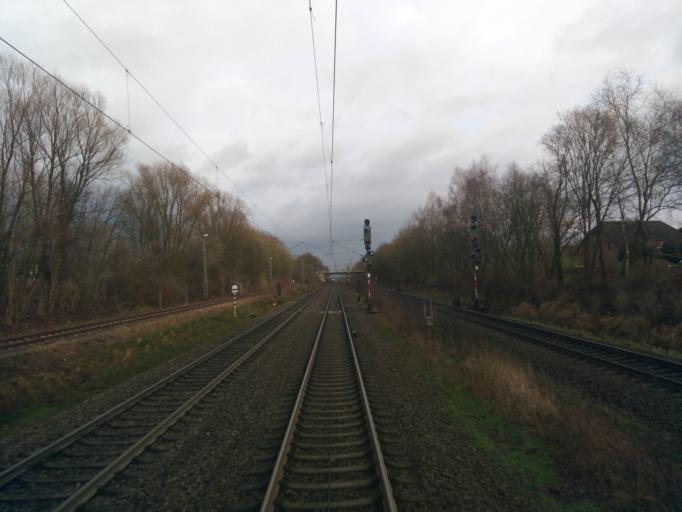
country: DE
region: Lower Saxony
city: Tostedt
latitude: 53.2671
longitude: 9.7212
